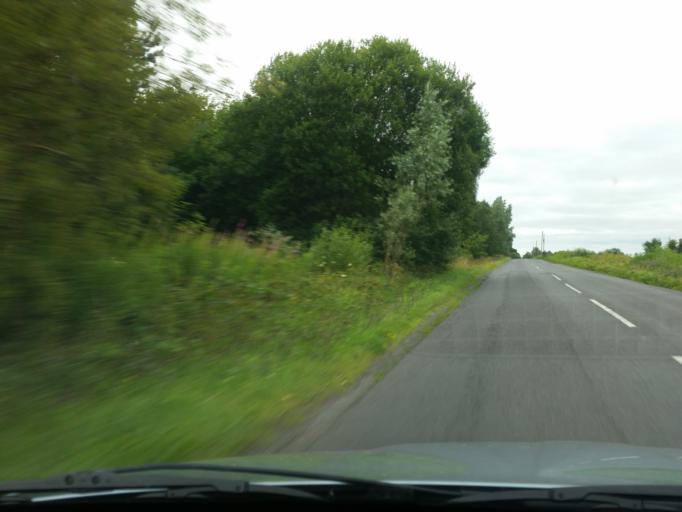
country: GB
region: Northern Ireland
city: Lisnaskea
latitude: 54.2372
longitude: -7.4522
